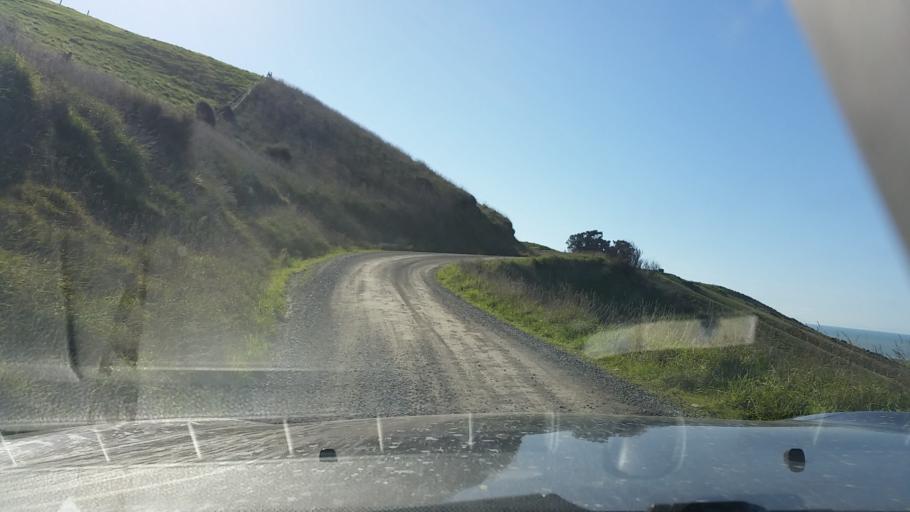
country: NZ
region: Marlborough
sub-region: Marlborough District
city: Blenheim
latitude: -41.6663
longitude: 174.1351
